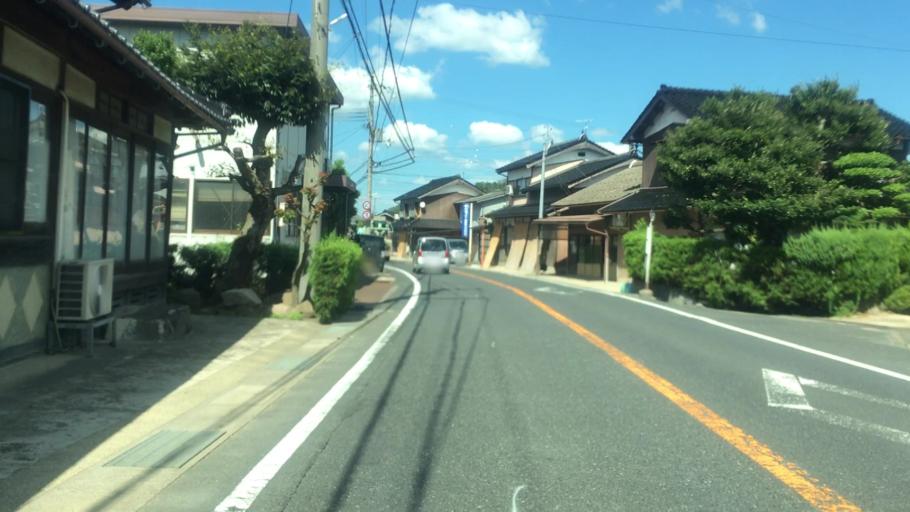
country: JP
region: Kyoto
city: Miyazu
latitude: 35.5913
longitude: 135.0400
